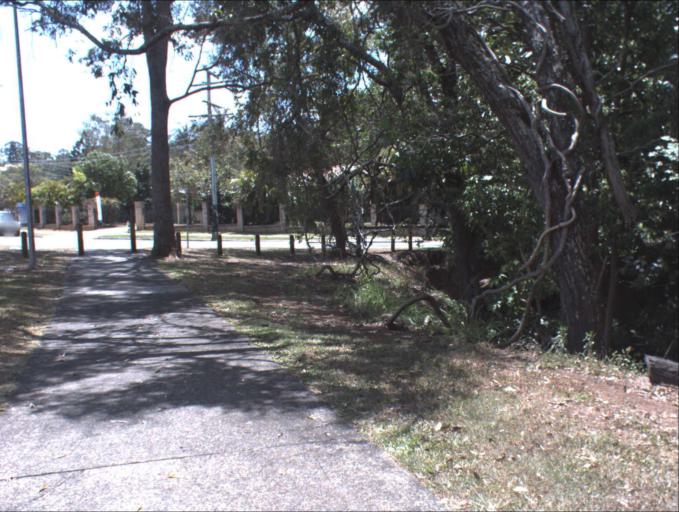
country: AU
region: Queensland
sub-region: Logan
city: Slacks Creek
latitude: -27.6395
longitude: 153.1577
